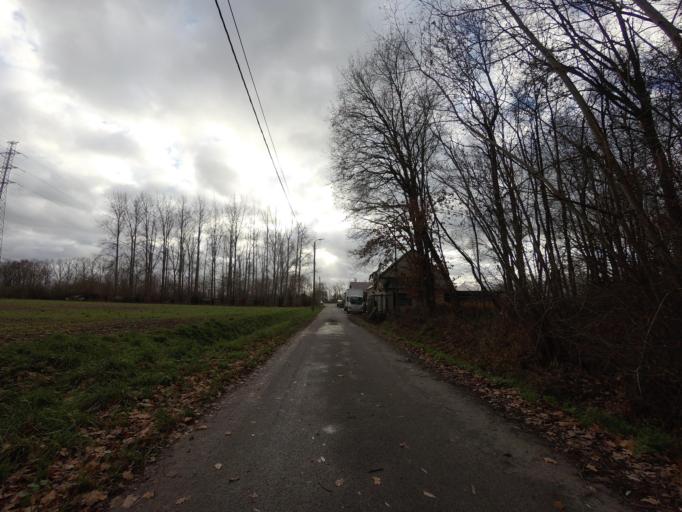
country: BE
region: Flanders
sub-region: Provincie Vlaams-Brabant
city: Haacht
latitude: 50.9545
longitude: 4.6112
